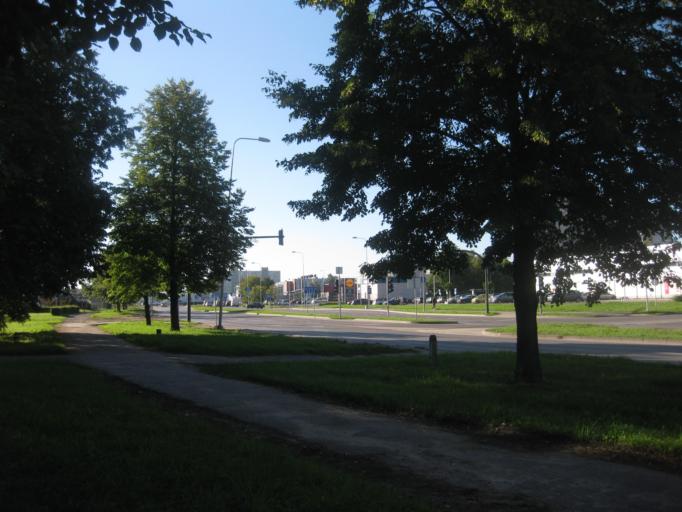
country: LT
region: Kauno apskritis
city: Dainava (Kaunas)
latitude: 54.9290
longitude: 23.9715
